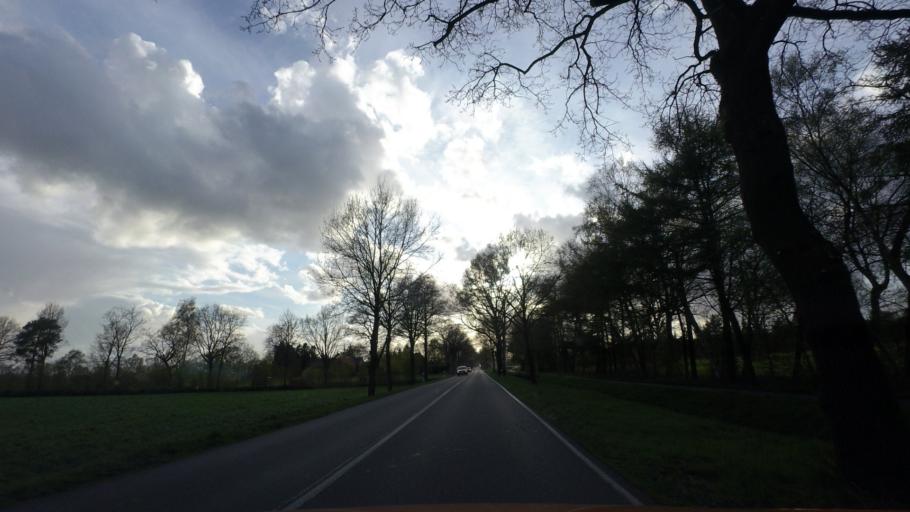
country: DE
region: Lower Saxony
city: Edewecht
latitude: 53.1229
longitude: 8.0508
